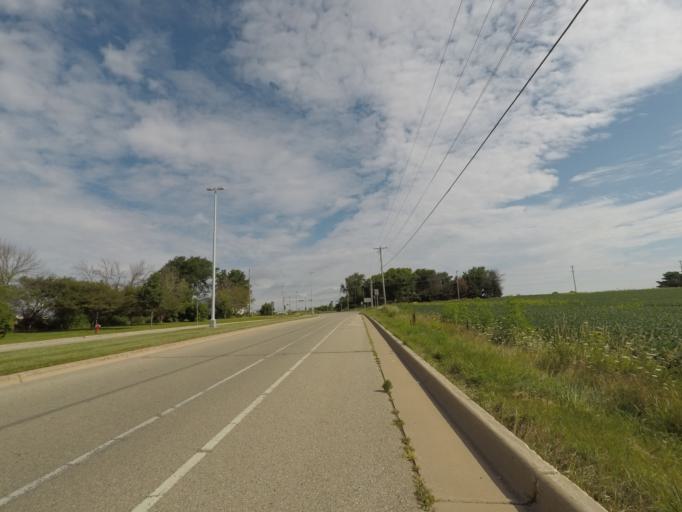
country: US
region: Wisconsin
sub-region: Dane County
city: Middleton
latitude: 43.0587
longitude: -89.5520
